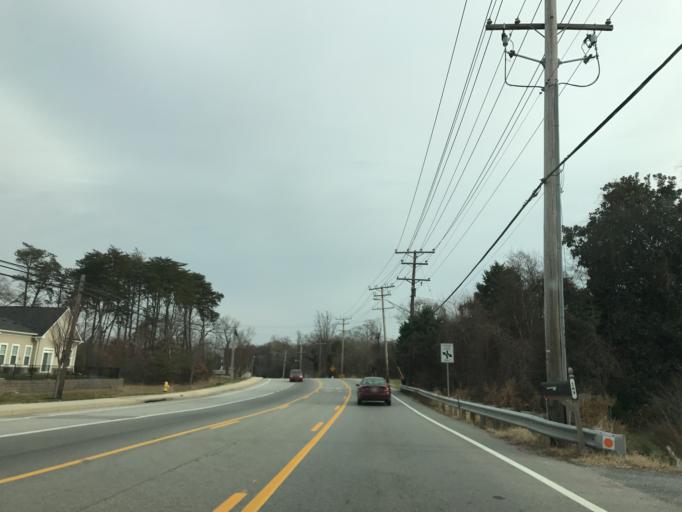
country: US
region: Maryland
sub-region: Anne Arundel County
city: Pasadena
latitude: 39.1320
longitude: -76.5733
